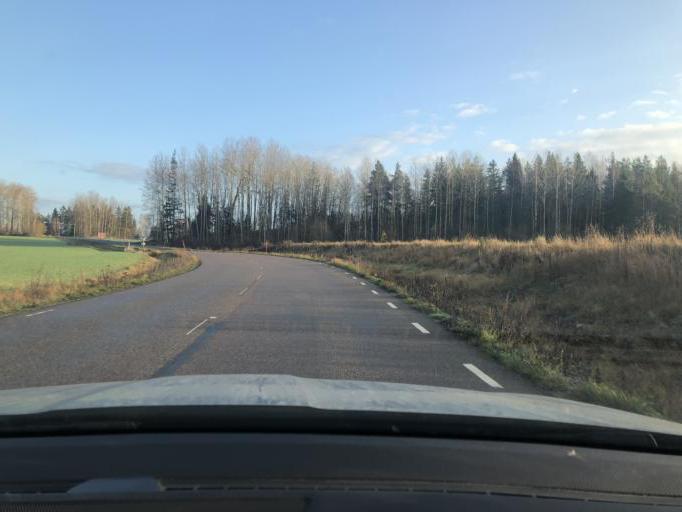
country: SE
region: Soedermanland
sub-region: Flens Kommun
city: Halleforsnas
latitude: 59.0297
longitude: 16.3931
